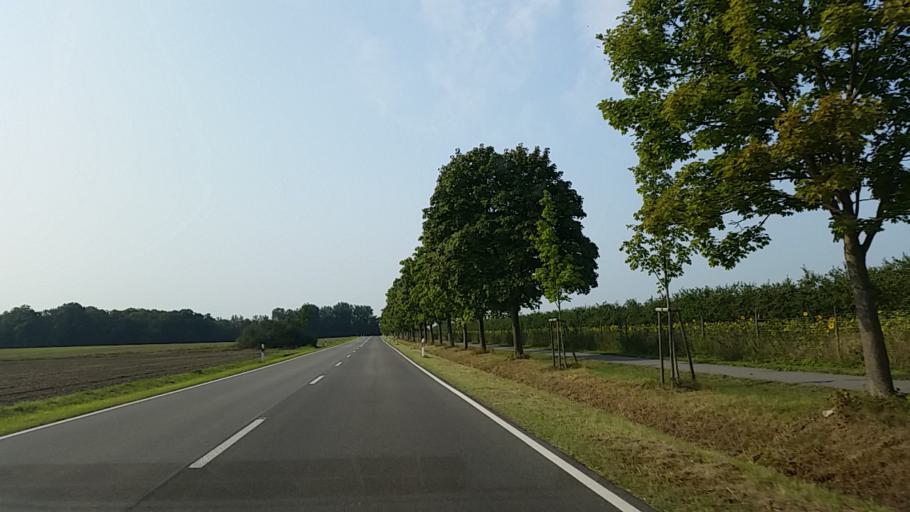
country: DE
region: Mecklenburg-Vorpommern
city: Lubtheen
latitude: 53.3879
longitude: 11.0883
